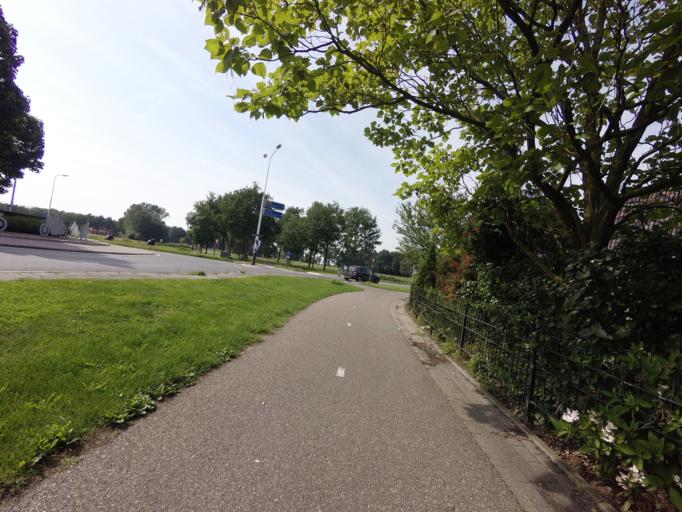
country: NL
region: Overijssel
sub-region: Gemeente Tubbergen
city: Tubbergen
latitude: 52.3989
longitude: 6.7828
